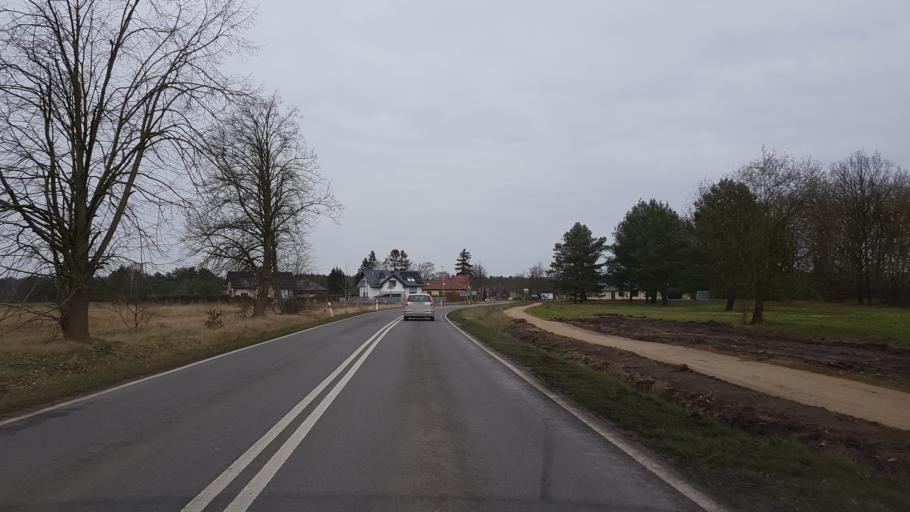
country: PL
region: West Pomeranian Voivodeship
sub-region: Powiat policki
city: Police
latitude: 53.6223
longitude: 14.5038
